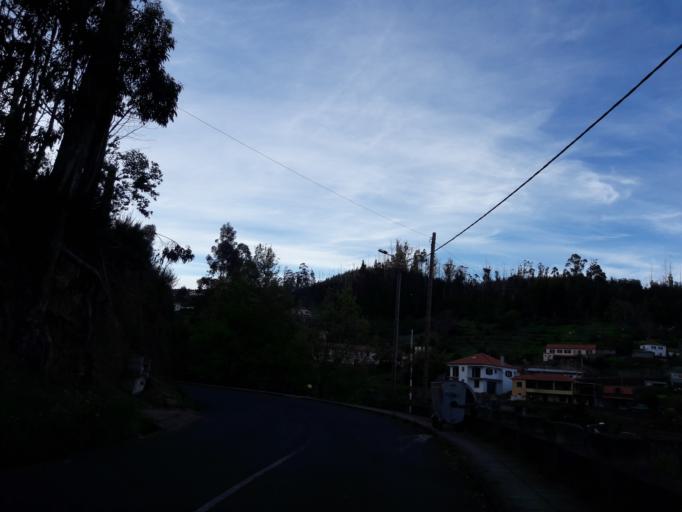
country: PT
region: Madeira
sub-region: Santa Cruz
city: Camacha
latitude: 32.6901
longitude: -16.8656
